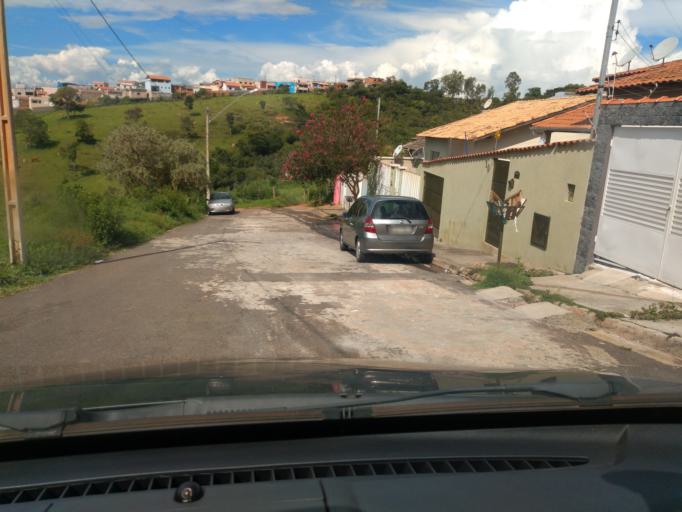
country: BR
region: Minas Gerais
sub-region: Tres Coracoes
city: Tres Coracoes
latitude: -21.6875
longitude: -45.2377
